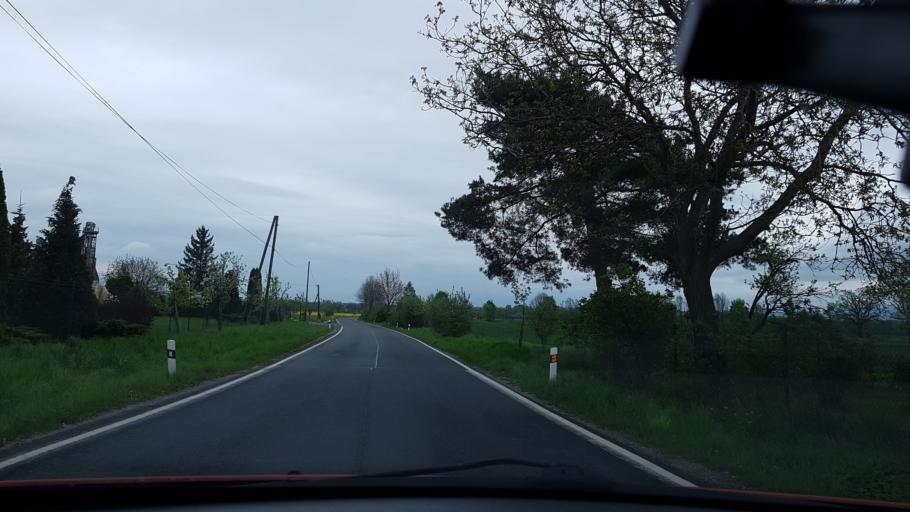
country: CZ
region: Olomoucky
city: Javornik
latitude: 50.3919
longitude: 17.0195
